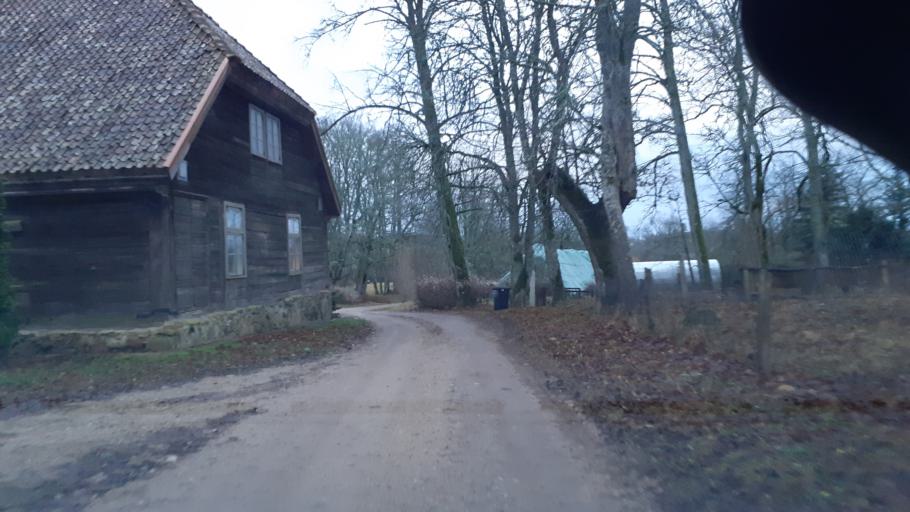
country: LV
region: Alsunga
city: Alsunga
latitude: 56.9052
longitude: 21.6954
